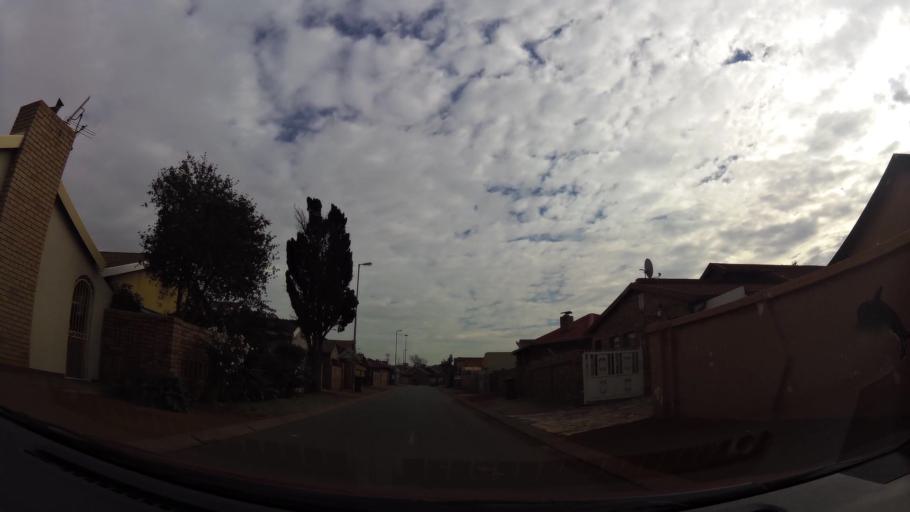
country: ZA
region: Gauteng
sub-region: City of Johannesburg Metropolitan Municipality
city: Soweto
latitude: -26.2701
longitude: 27.8353
